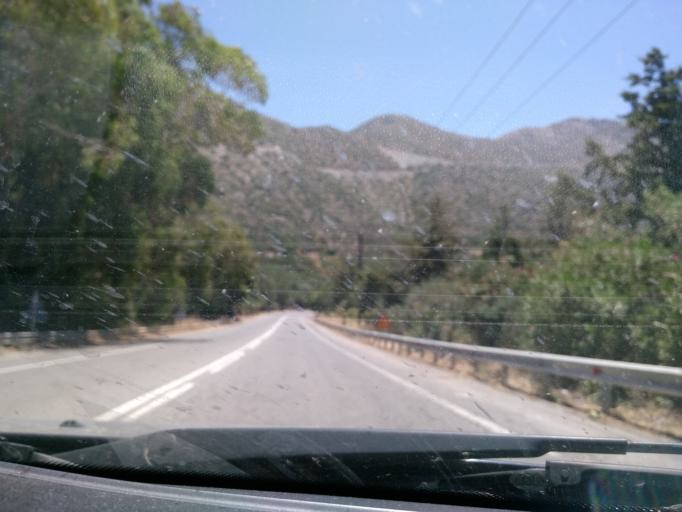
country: GR
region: Crete
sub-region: Nomos Rethymnis
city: Anogeia
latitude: 35.3903
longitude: 24.8859
